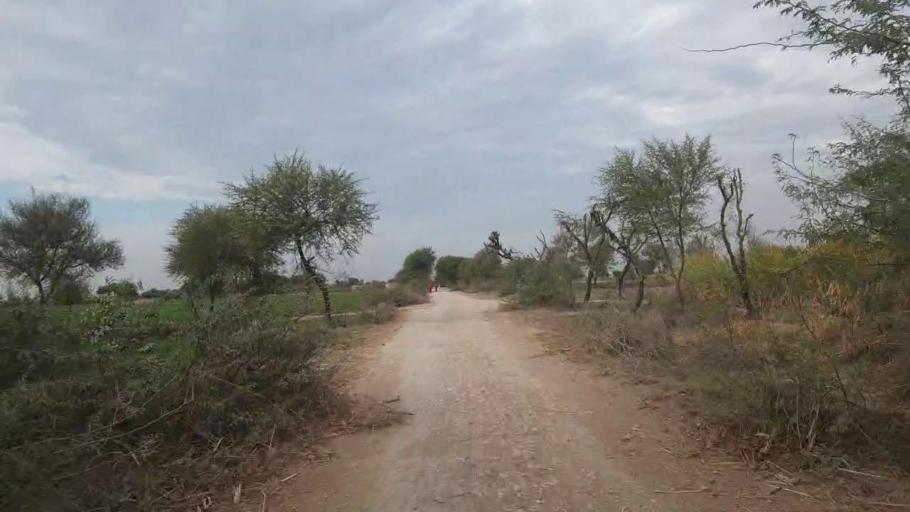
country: PK
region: Sindh
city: Jhol
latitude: 26.0075
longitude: 68.8725
